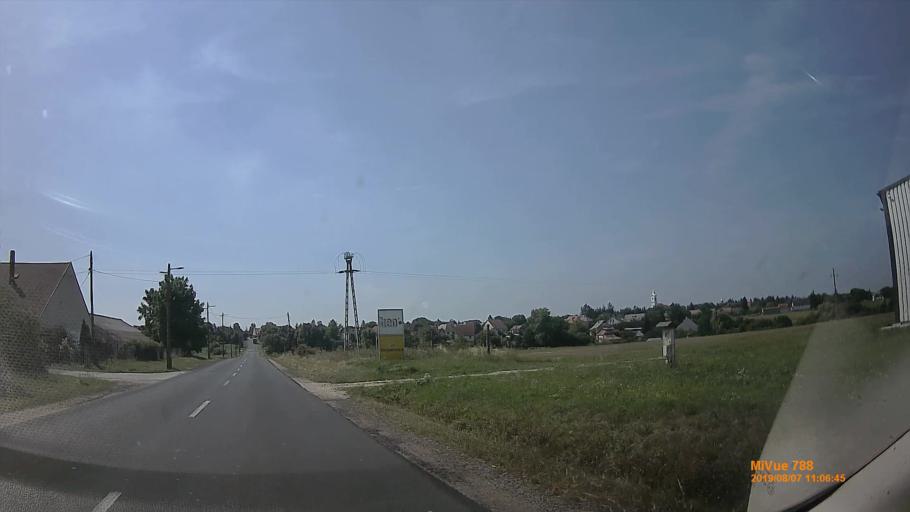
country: HU
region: Veszprem
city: Devecser
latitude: 47.0099
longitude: 17.4552
